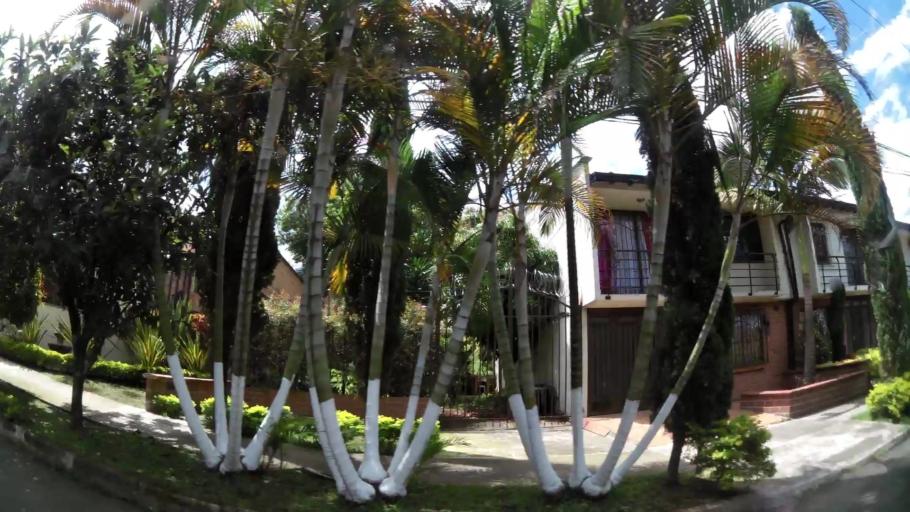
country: CO
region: Antioquia
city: La Estrella
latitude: 6.1584
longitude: -75.6371
